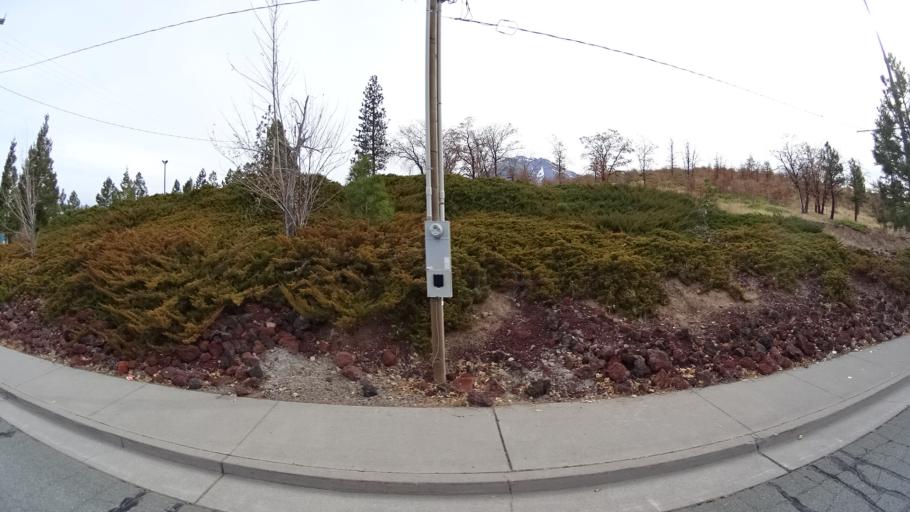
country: US
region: California
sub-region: Siskiyou County
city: Weed
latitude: 41.4265
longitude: -122.3814
